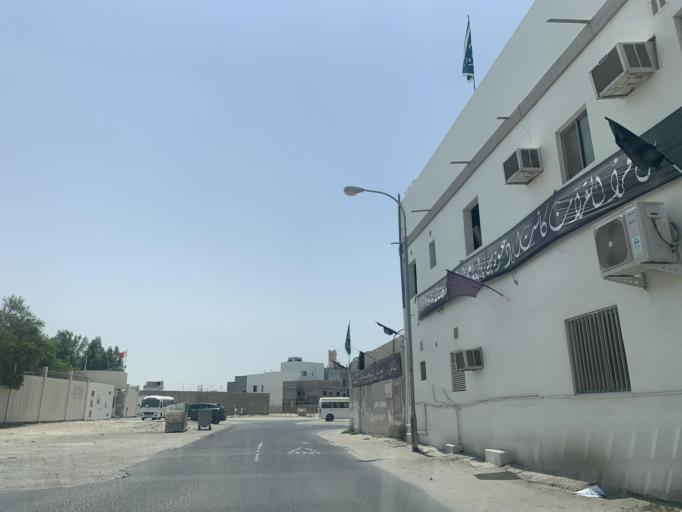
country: BH
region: Central Governorate
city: Madinat Hamad
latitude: 26.1450
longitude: 50.5013
